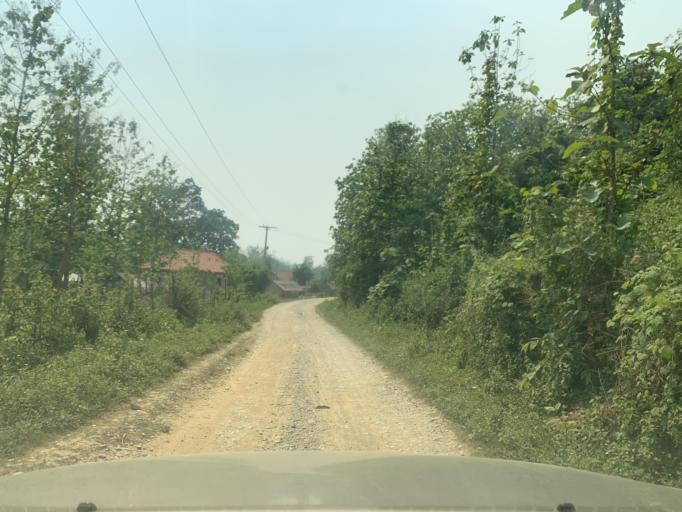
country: LA
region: Louangphabang
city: Louangphabang
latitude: 19.8841
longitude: 102.2541
